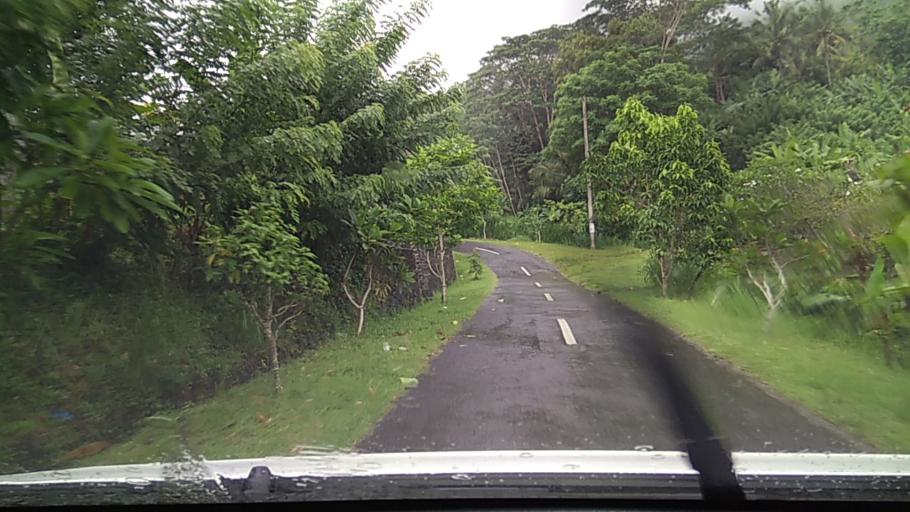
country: ID
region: Bali
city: Tiyingtali Kelod
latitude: -8.4071
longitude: 115.6267
